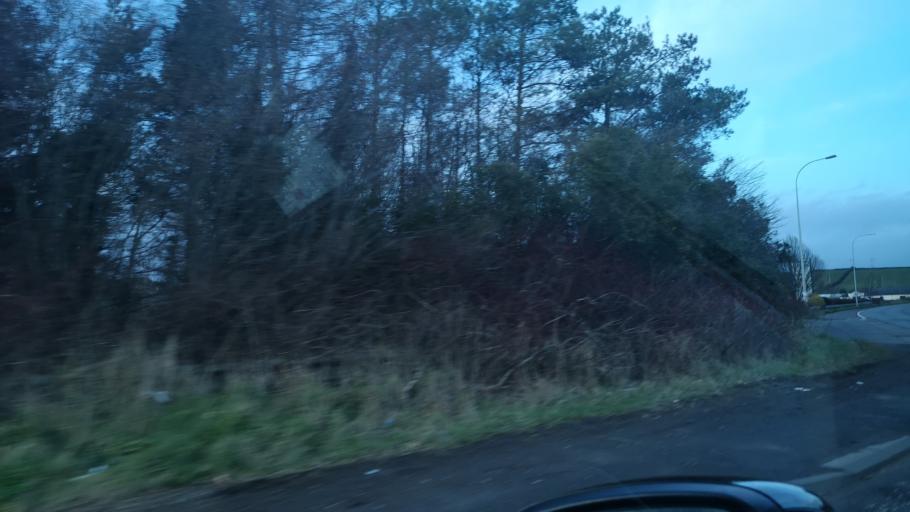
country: GB
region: Northern Ireland
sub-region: Newry and Mourne District
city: Newry
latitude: 54.1951
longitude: -6.3475
